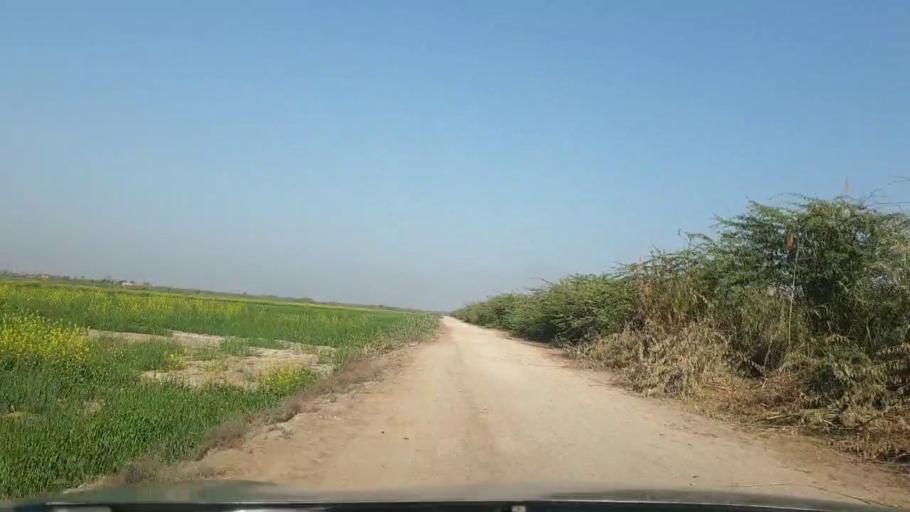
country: PK
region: Sindh
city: Berani
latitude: 25.6591
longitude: 68.9122
